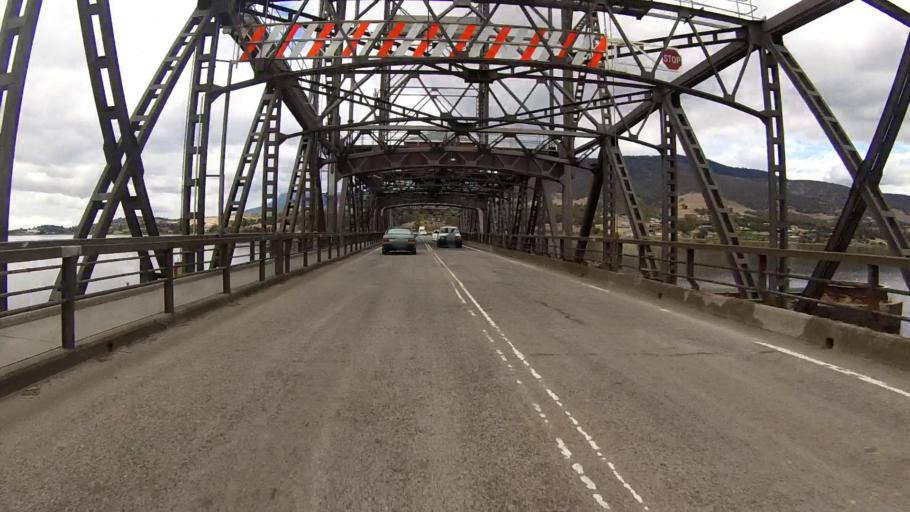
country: AU
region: Tasmania
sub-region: Brighton
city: Bridgewater
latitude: -42.7401
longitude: 147.2265
